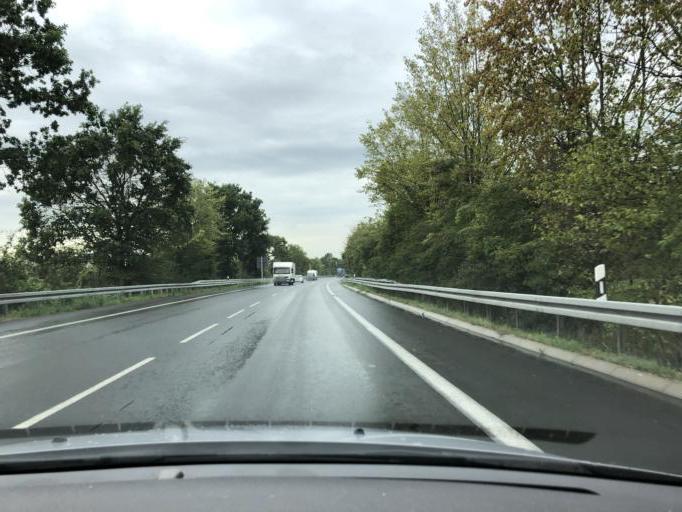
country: DE
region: North Rhine-Westphalia
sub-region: Regierungsbezirk Dusseldorf
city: Schermbeck
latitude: 51.6862
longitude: 6.8766
